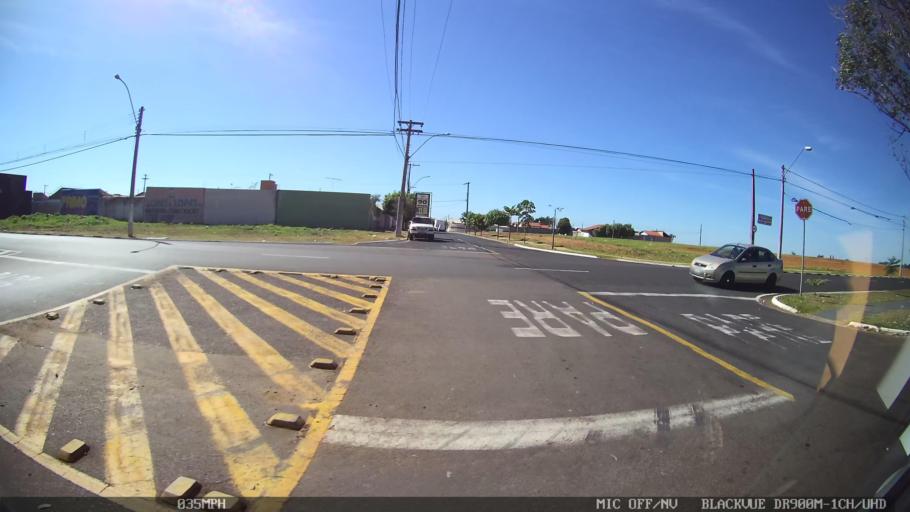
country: BR
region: Sao Paulo
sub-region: Franca
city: Franca
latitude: -20.5589
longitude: -47.3595
